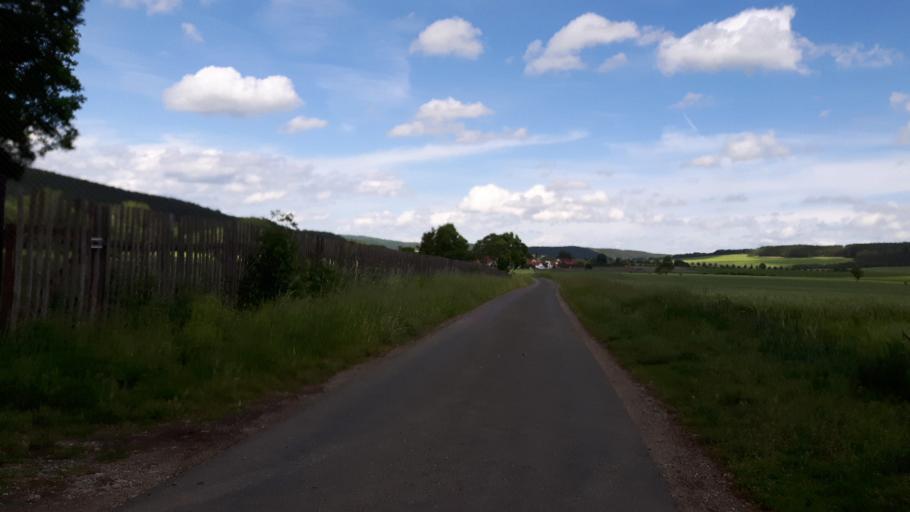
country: DE
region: Thuringia
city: Witzleben
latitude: 50.7849
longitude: 11.1292
